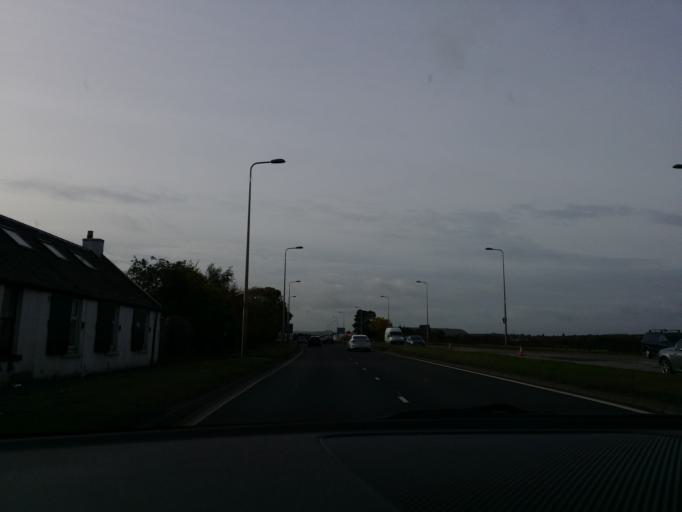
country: GB
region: Scotland
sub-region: Edinburgh
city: Newbridge
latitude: 55.9389
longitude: -3.3935
